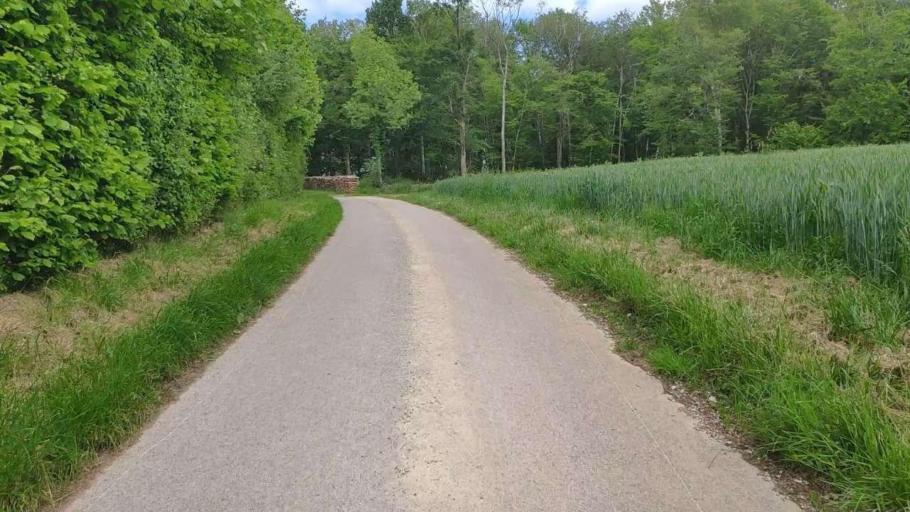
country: FR
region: Franche-Comte
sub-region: Departement du Jura
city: Poligny
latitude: 46.7702
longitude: 5.6555
